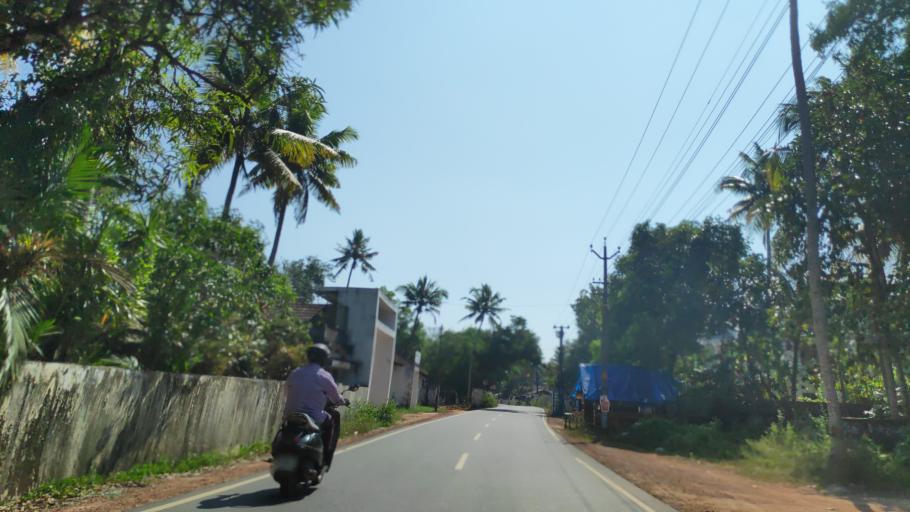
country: IN
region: Kerala
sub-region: Alappuzha
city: Shertallai
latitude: 9.6377
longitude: 76.3154
